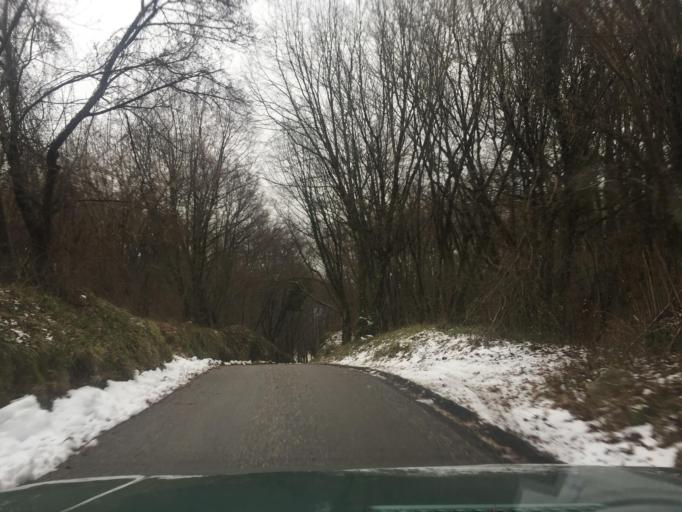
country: SI
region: Kanal
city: Kanal
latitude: 46.0728
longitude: 13.6890
